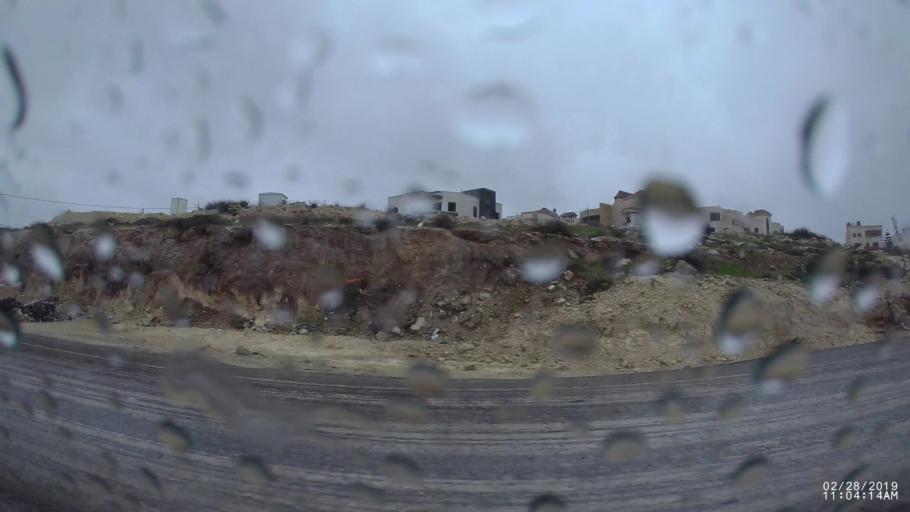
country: JO
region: Amman
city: Al Jubayhah
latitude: 32.0124
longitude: 35.8975
